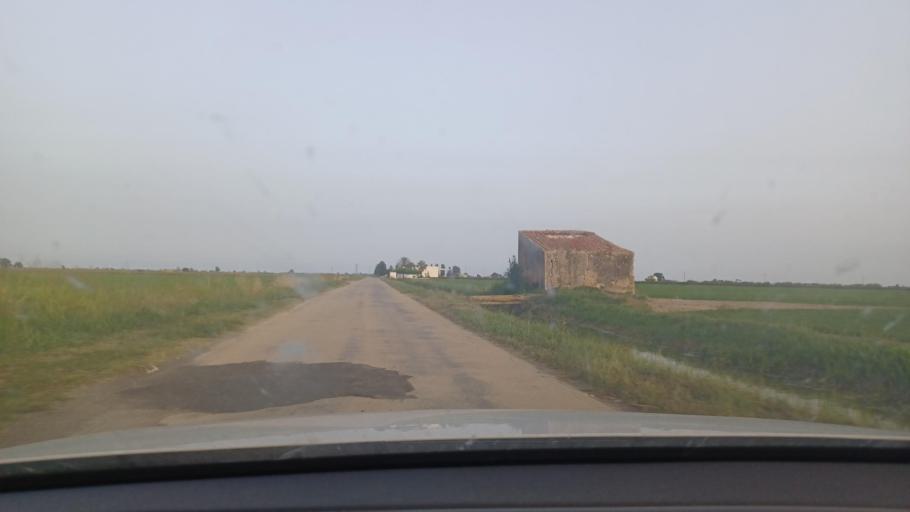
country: ES
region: Catalonia
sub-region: Provincia de Tarragona
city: Deltebre
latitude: 40.6863
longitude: 0.6537
